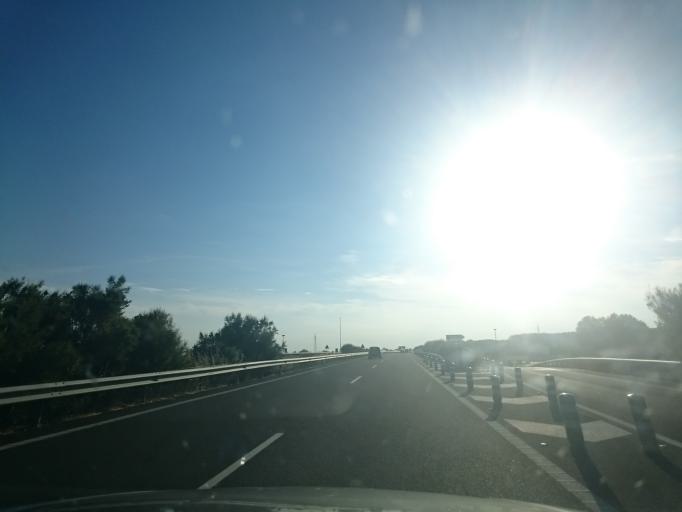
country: ES
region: Castille and Leon
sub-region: Provincia de Palencia
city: Carrion de los Condes
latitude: 42.3497
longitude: -4.6200
